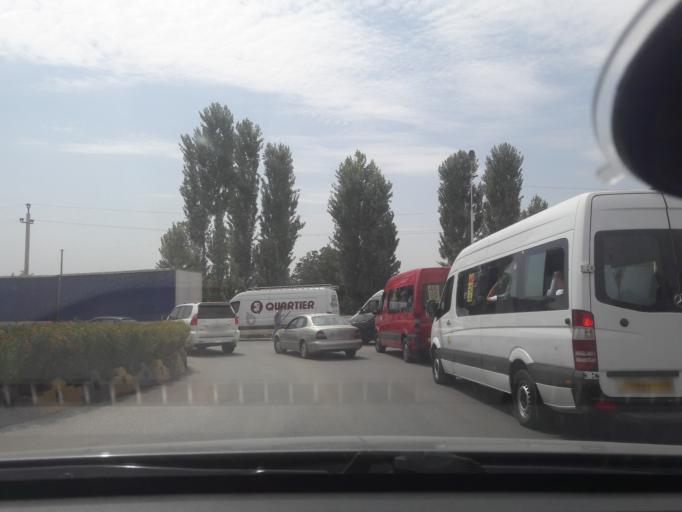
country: TJ
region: Dushanbe
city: Dushanbe
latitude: 38.5829
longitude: 68.7061
